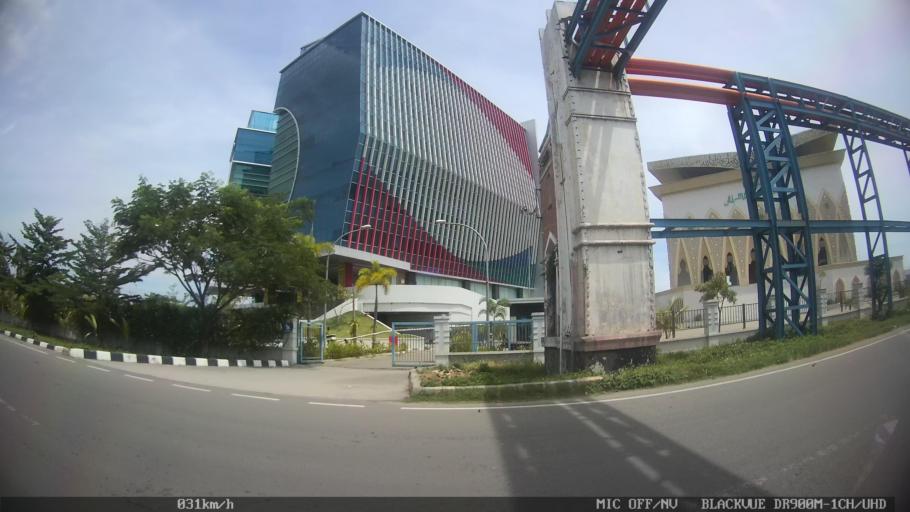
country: ID
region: North Sumatra
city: Belawan
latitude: 3.7812
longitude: 98.6887
